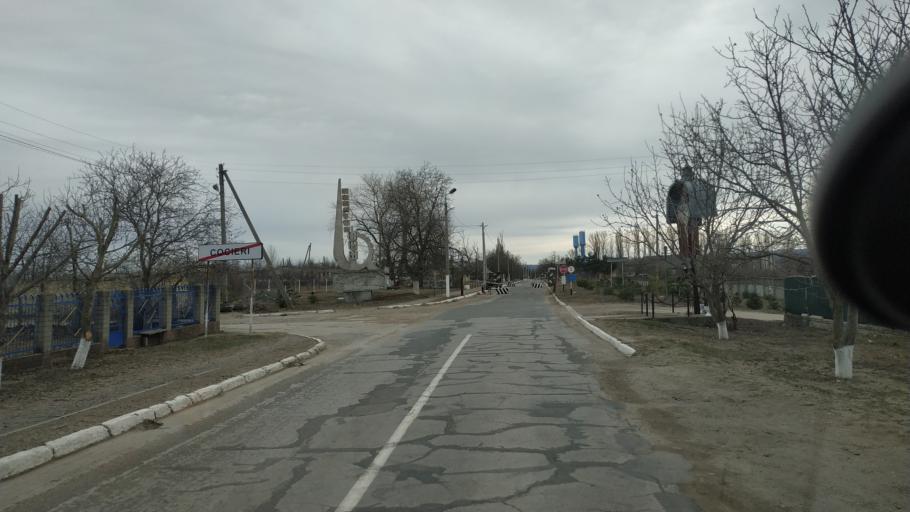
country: MD
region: Telenesti
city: Cocieri
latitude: 47.2967
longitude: 29.1168
